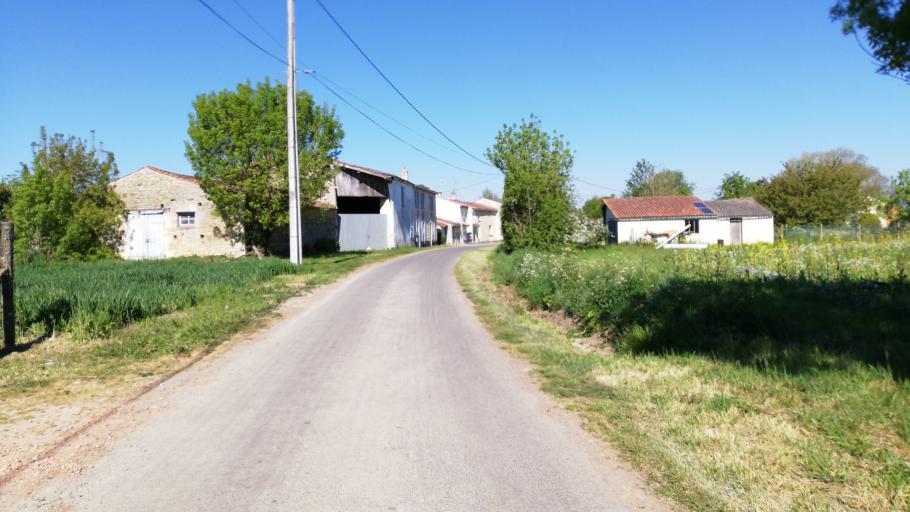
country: FR
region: Pays de la Loire
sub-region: Departement de la Vendee
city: Maillezais
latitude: 46.3273
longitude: -0.7487
